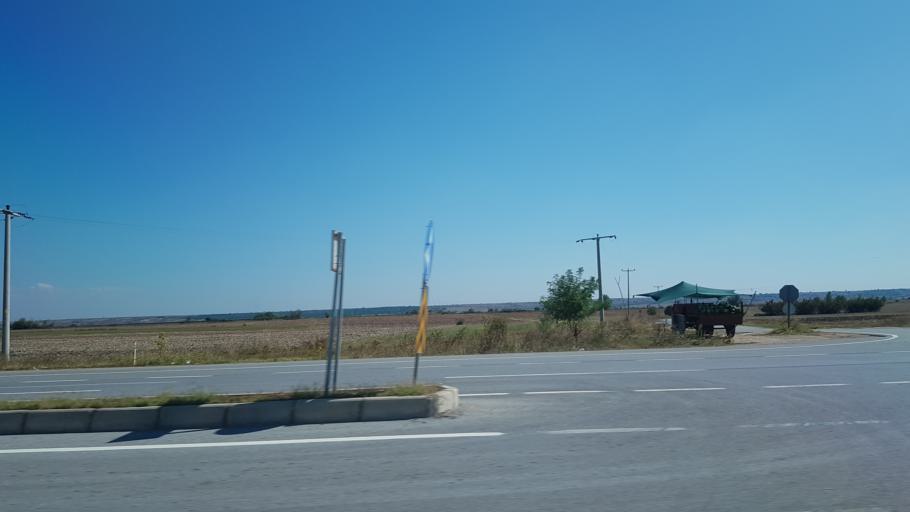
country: TR
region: Kirklareli
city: Inece
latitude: 41.5691
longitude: 27.1459
